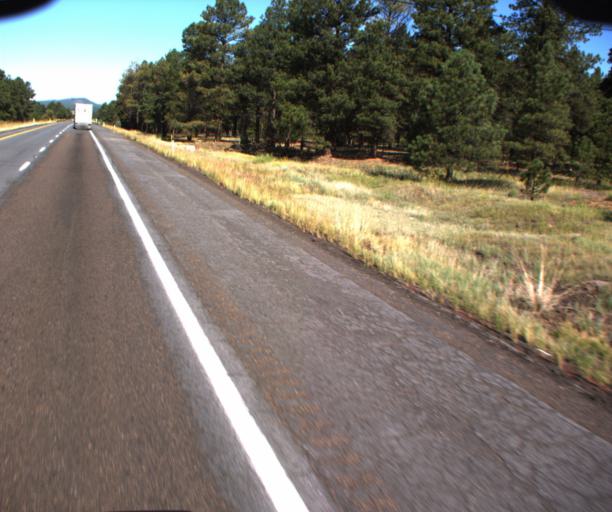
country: US
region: Arizona
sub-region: Coconino County
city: Parks
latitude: 35.2549
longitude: -112.0079
